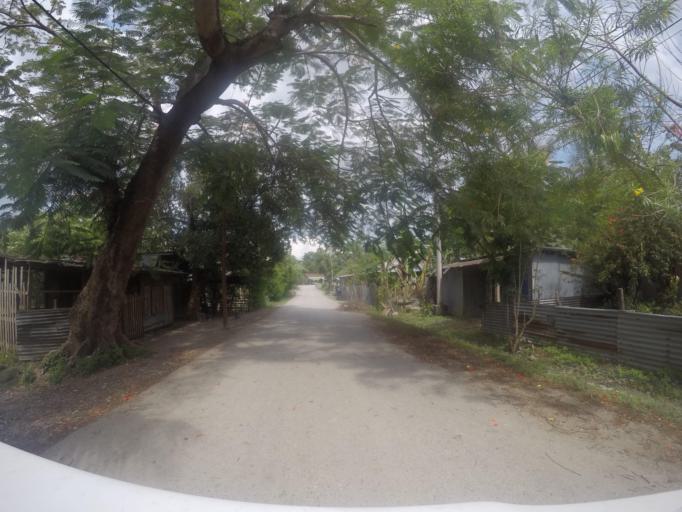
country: TL
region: Viqueque
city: Viqueque
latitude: -8.8580
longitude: 126.3640
